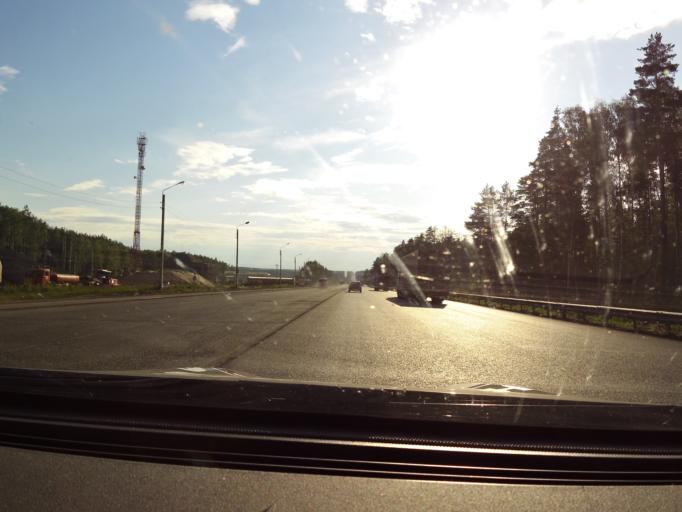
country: RU
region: Vladimir
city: Melekhovo
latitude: 56.2140
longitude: 41.3507
